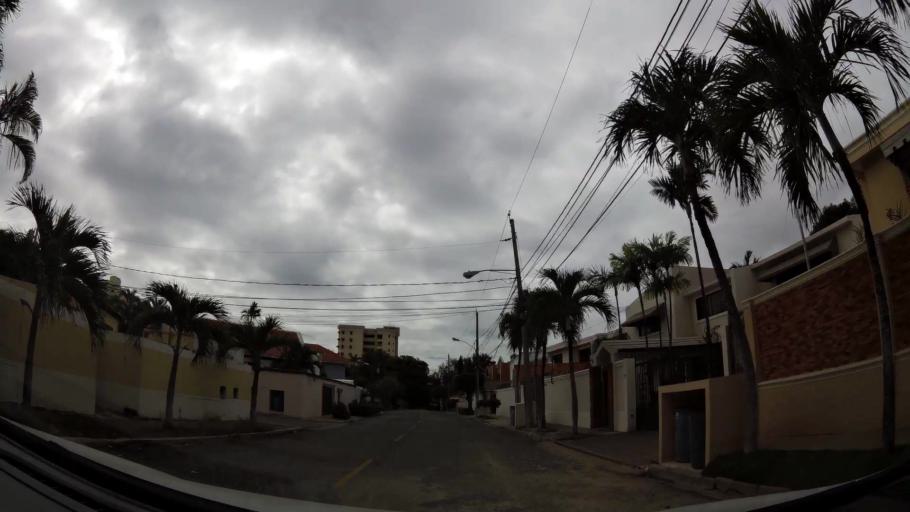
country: DO
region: Nacional
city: Bella Vista
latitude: 18.4511
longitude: -69.9433
